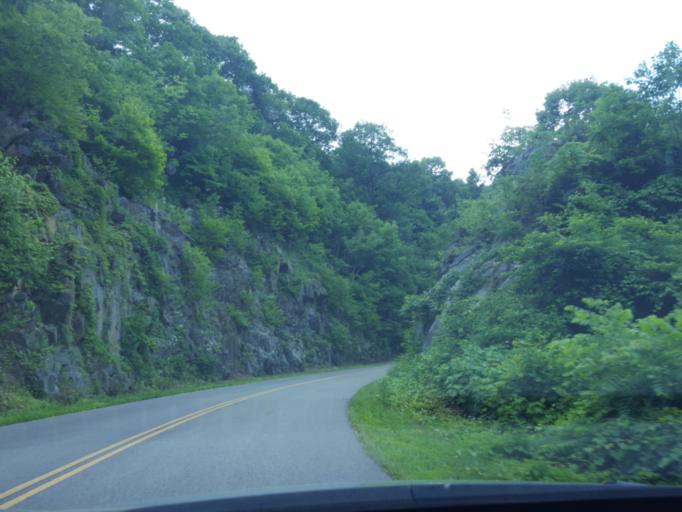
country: US
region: Virginia
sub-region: Nelson County
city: Nellysford
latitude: 37.9523
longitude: -78.9105
